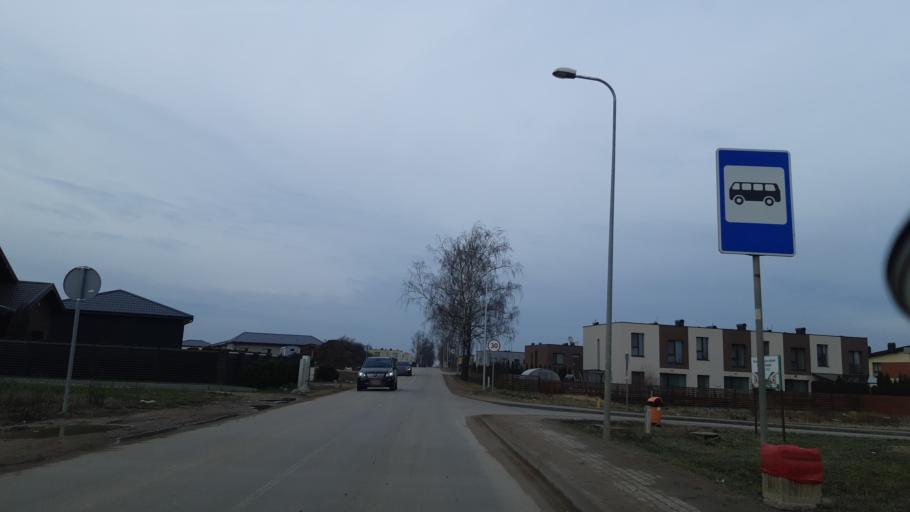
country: LT
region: Kauno apskritis
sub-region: Kauno rajonas
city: Akademija (Kaunas)
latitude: 54.9456
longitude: 23.8287
